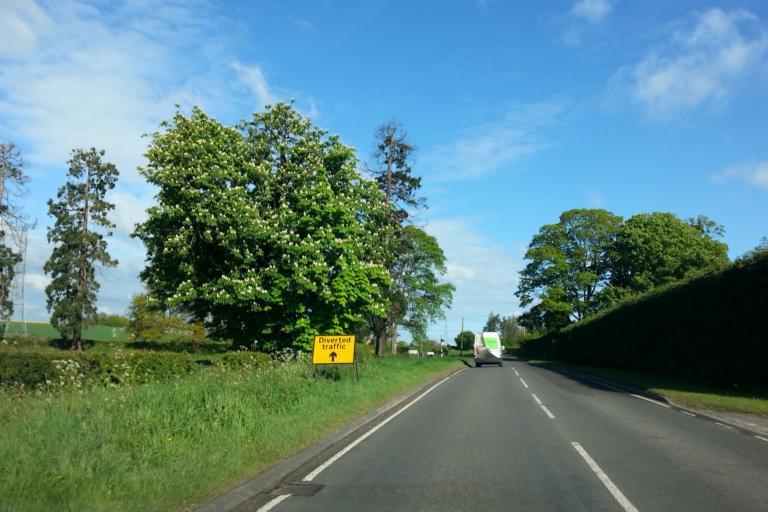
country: GB
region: England
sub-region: Nottinghamshire
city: Cotgrave
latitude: 52.9215
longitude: -1.0160
